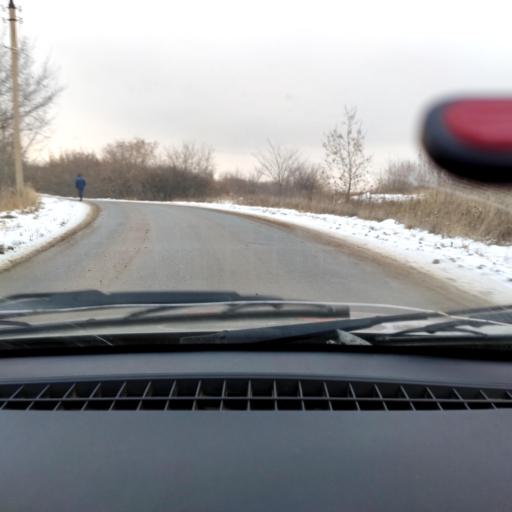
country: RU
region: Bashkortostan
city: Blagoveshchensk
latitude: 54.8900
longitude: 56.0479
